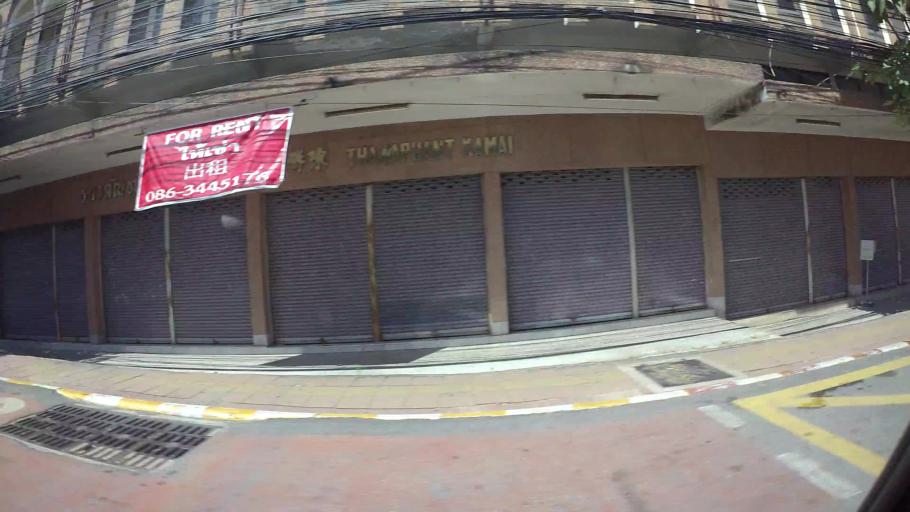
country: TH
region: Chon Buri
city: Phatthaya
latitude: 12.9322
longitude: 100.8993
